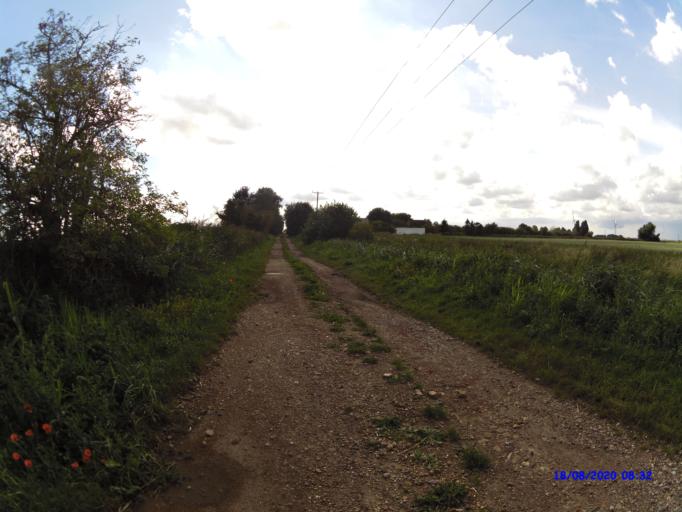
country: GB
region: England
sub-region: Cambridgeshire
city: Ramsey
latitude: 52.4994
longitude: -0.0838
